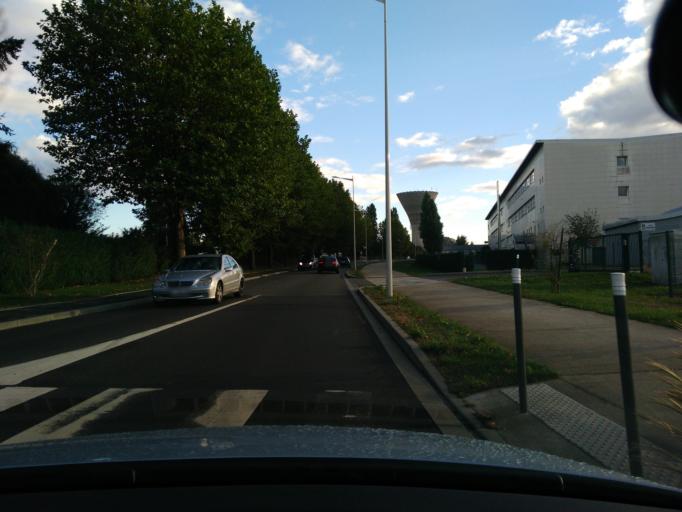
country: FR
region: Haute-Normandie
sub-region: Departement de l'Eure
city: Evreux
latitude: 49.0197
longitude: 1.1715
